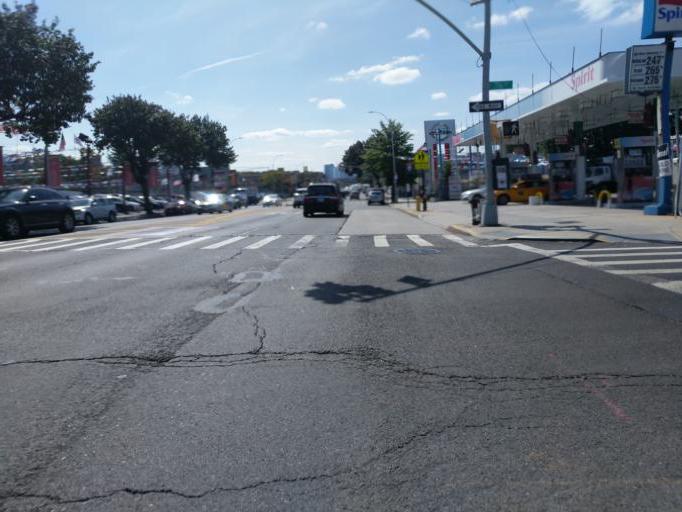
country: US
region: New York
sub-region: Queens County
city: Long Island City
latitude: 40.7551
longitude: -73.8909
